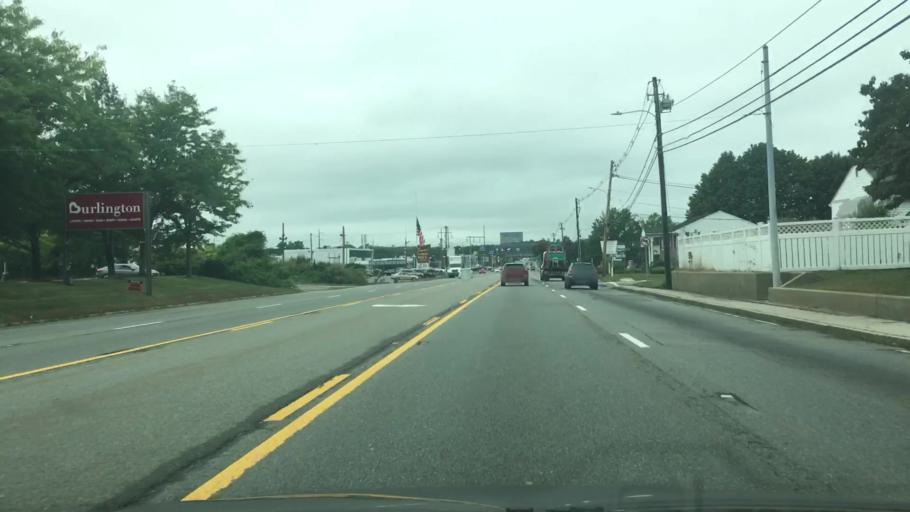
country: US
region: Massachusetts
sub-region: Essex County
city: Danvers
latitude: 42.5511
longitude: -70.9568
